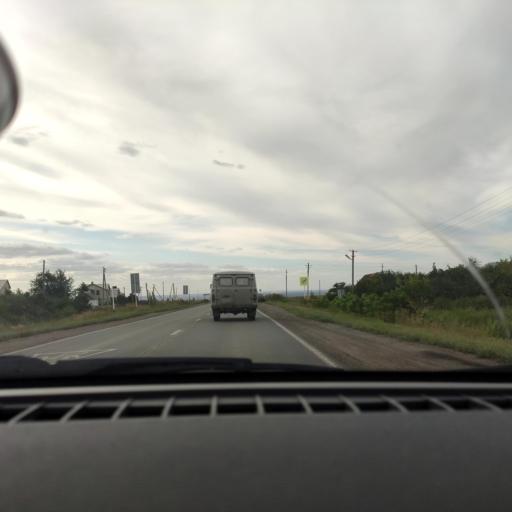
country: RU
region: Samara
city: Krasnyy Yar
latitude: 53.4453
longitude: 50.5269
